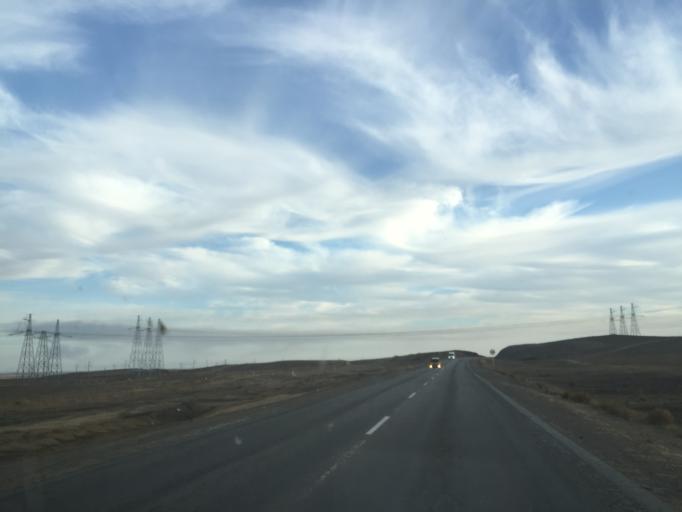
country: KZ
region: Almaty Oblysy
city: Ulken
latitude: 45.1396
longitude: 73.9624
